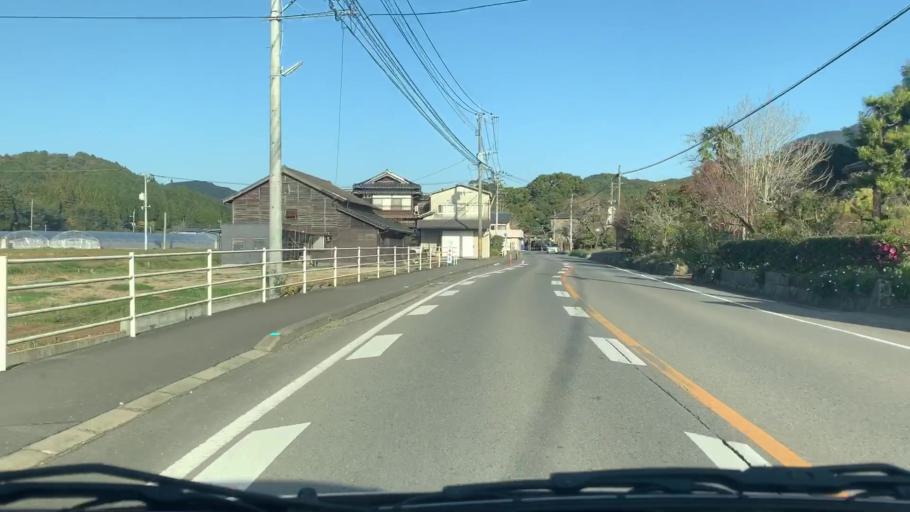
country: JP
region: Saga Prefecture
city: Takeocho-takeo
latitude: 33.2225
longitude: 130.0261
